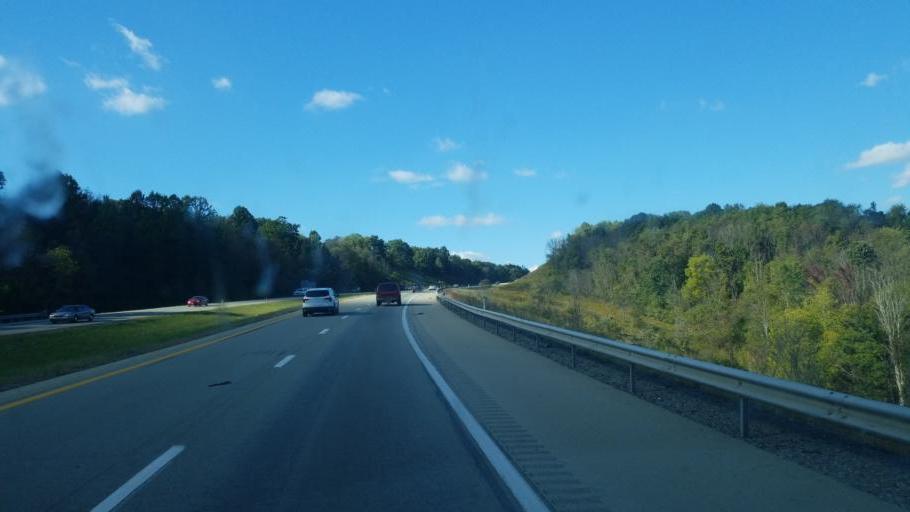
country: US
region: Pennsylvania
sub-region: Greene County
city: Morrisville
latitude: 39.8312
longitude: -80.1105
